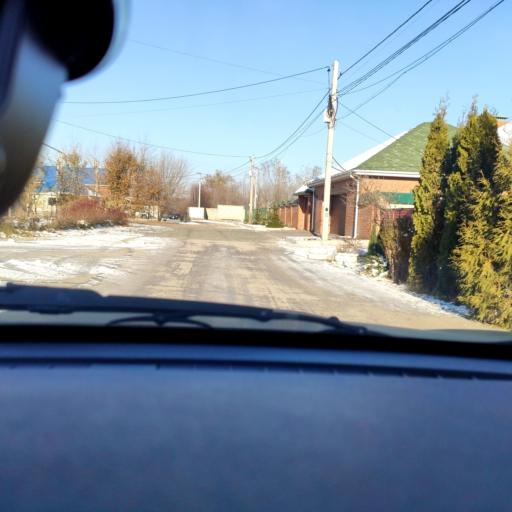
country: RU
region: Samara
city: Tol'yatti
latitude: 53.5439
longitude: 49.3761
